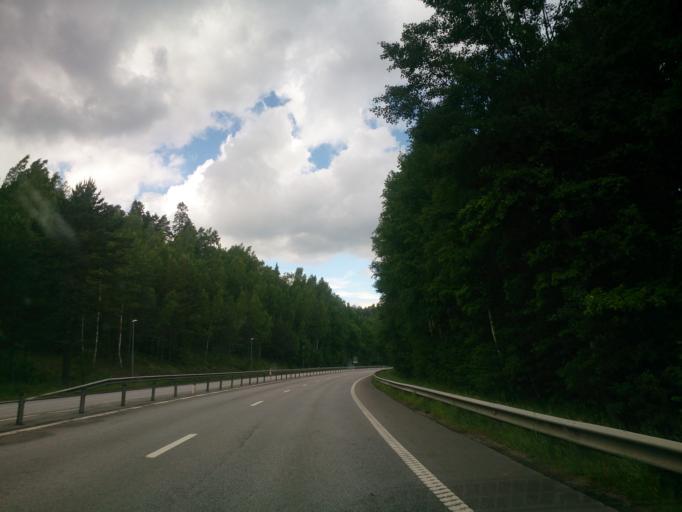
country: SE
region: OEstergoetland
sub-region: Norrkopings Kommun
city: Jursla
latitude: 58.6767
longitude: 16.1501
